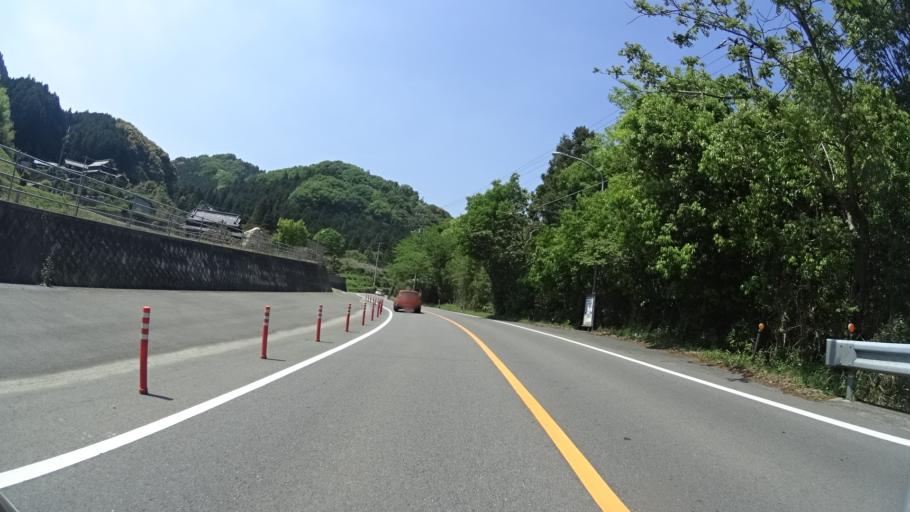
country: JP
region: Ehime
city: Hojo
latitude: 33.9687
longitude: 132.9041
